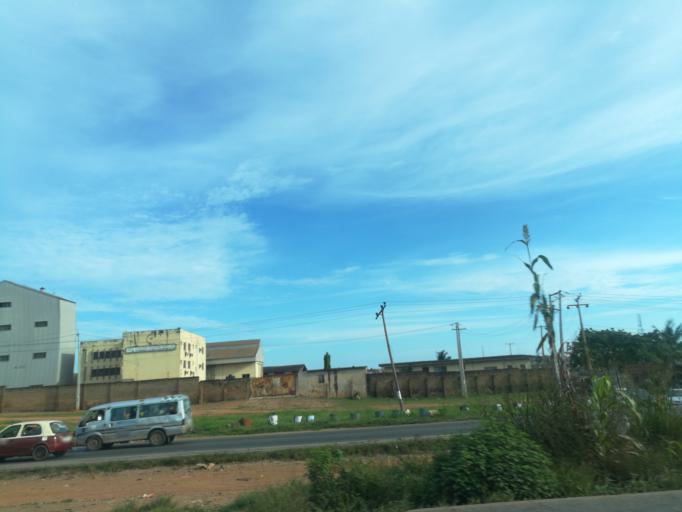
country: NG
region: Oyo
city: Ibadan
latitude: 7.3421
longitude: 3.9088
